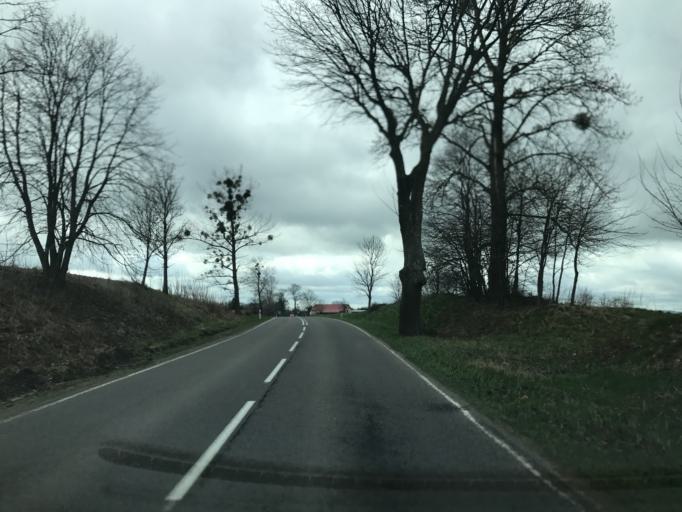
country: PL
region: Warmian-Masurian Voivodeship
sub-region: Powiat ostrodzki
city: Gierzwald
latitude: 53.4972
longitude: 20.1485
